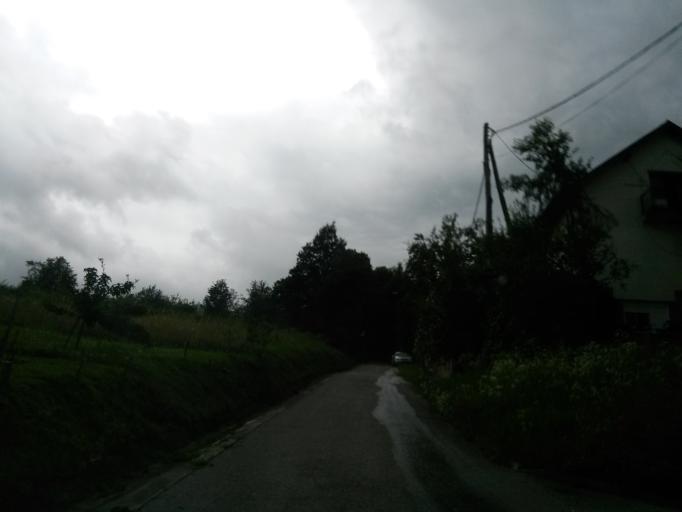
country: HR
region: Sisacko-Moslavacka
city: Gvozd
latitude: 45.2954
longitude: 15.9664
